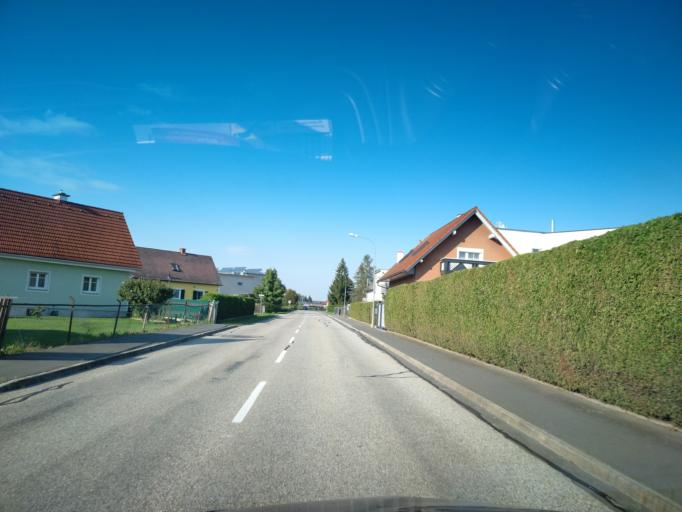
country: AT
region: Styria
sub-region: Politischer Bezirk Leibnitz
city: Kaindorf an der Sulm
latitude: 46.7997
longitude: 15.5392
